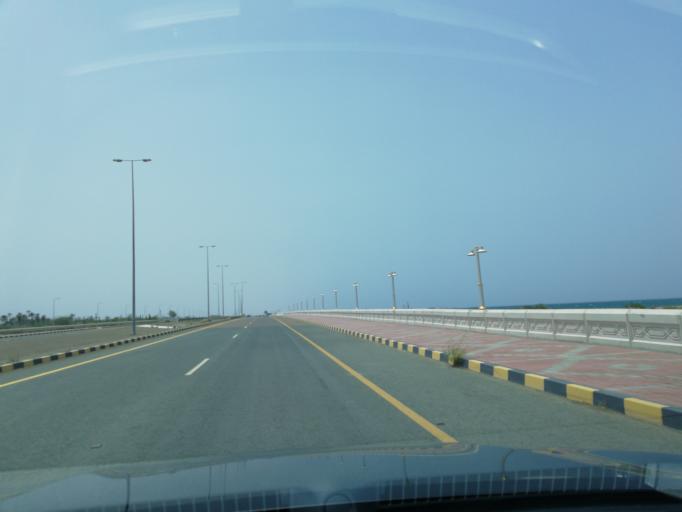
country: OM
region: Al Batinah
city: Al Liwa'
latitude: 24.6275
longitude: 56.5296
